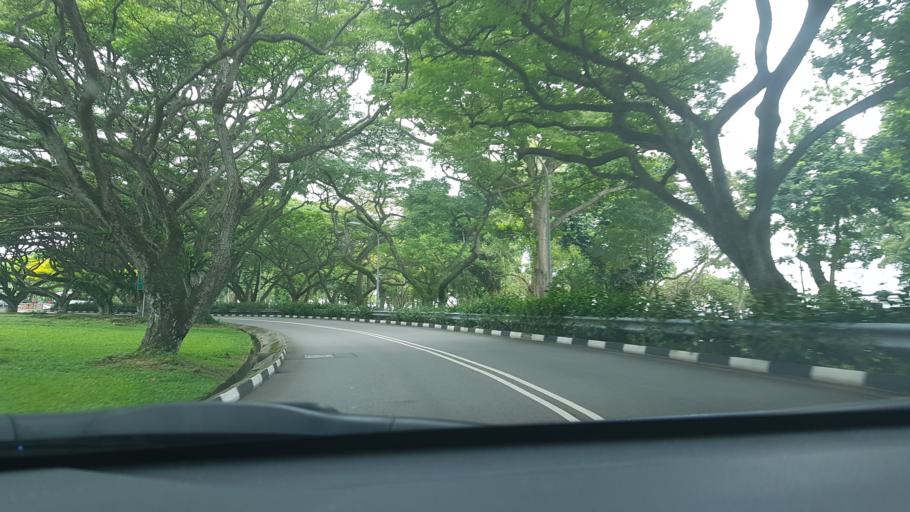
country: SG
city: Singapore
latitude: 1.2998
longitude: 103.9099
